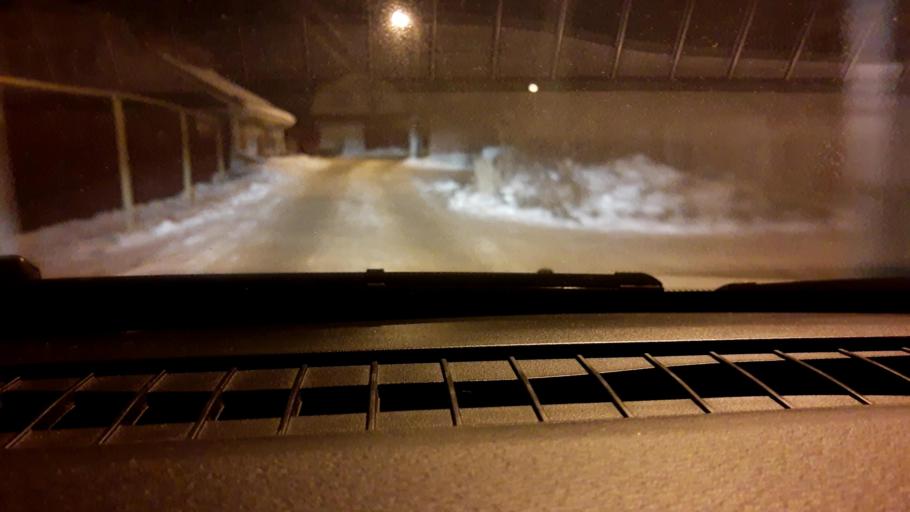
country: RU
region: Nizjnij Novgorod
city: Nizhniy Novgorod
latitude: 56.2324
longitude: 43.9855
